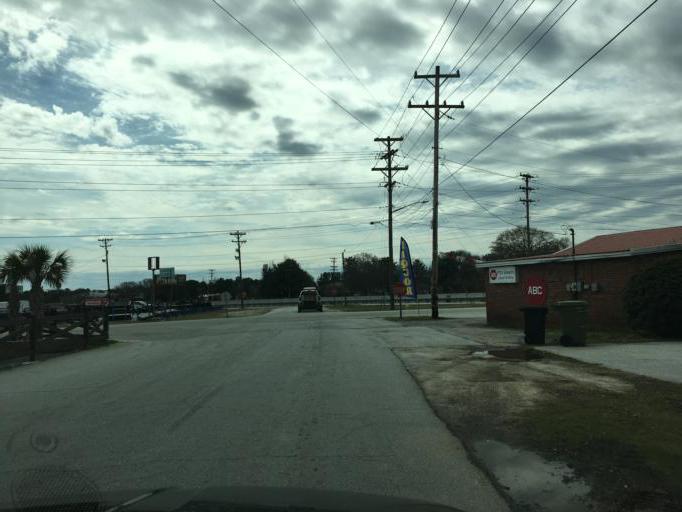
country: US
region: South Carolina
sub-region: Greenville County
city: Fountain Inn
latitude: 34.6916
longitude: -82.2215
